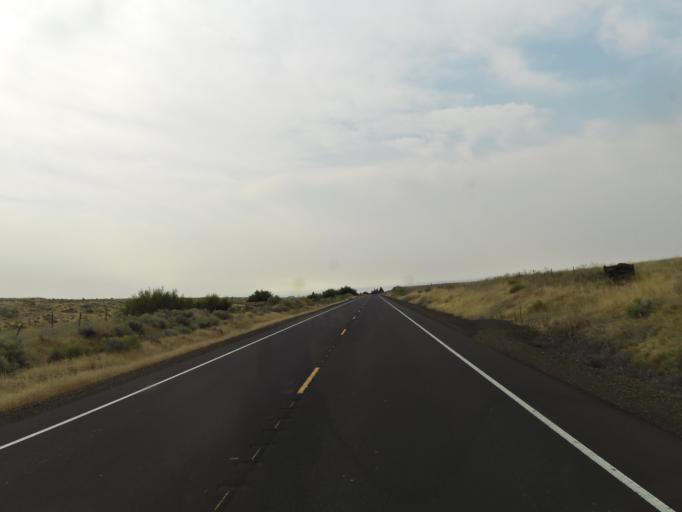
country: US
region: Oregon
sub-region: Sherman County
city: Moro
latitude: 45.3388
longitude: -120.7735
